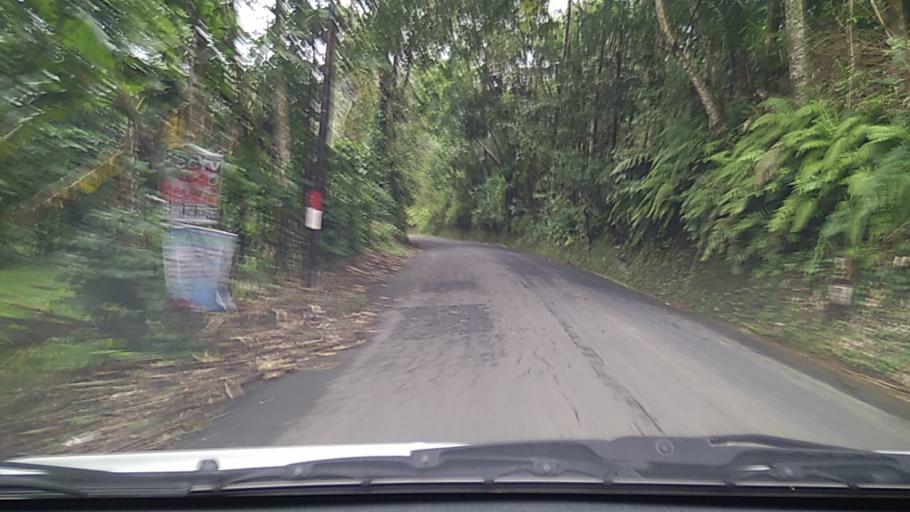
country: ID
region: Bali
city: Banjar Manukayaanyar
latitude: -8.4191
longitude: 115.3042
